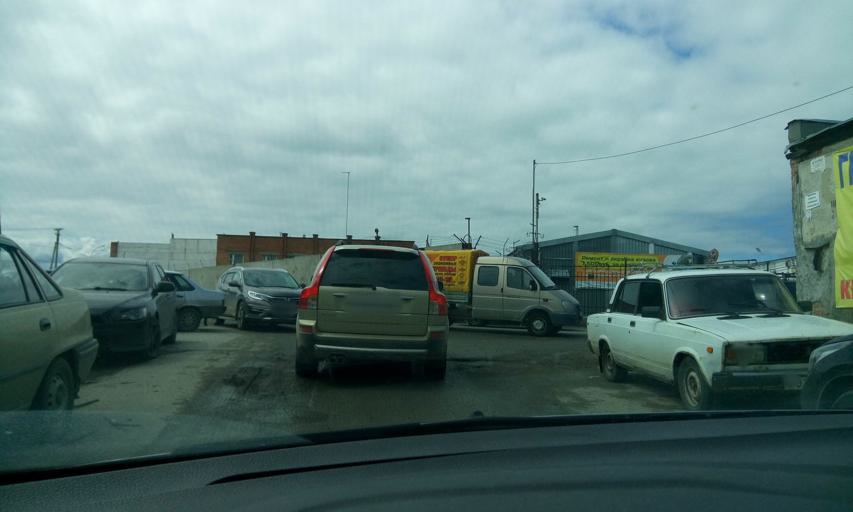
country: RU
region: Sverdlovsk
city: Yekaterinburg
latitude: 56.8672
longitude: 60.5962
